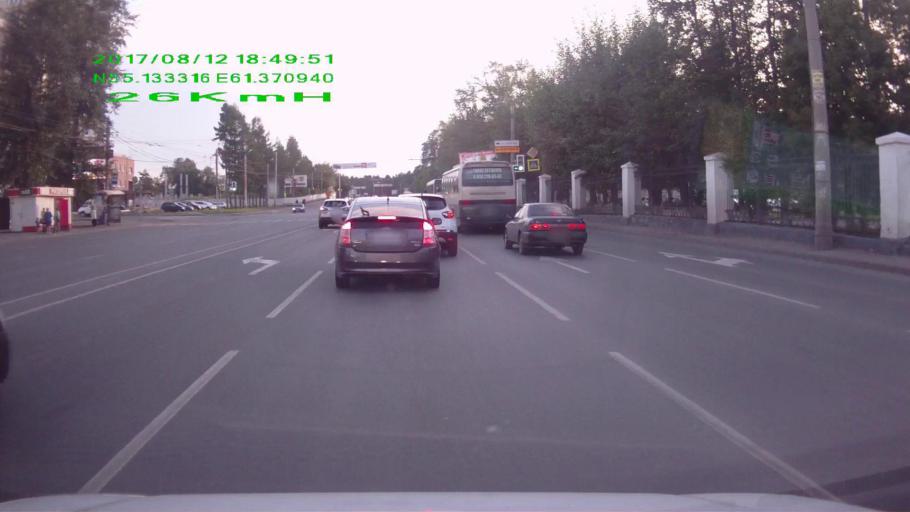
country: RU
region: Chelyabinsk
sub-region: Gorod Chelyabinsk
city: Chelyabinsk
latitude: 55.1295
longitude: 61.3662
